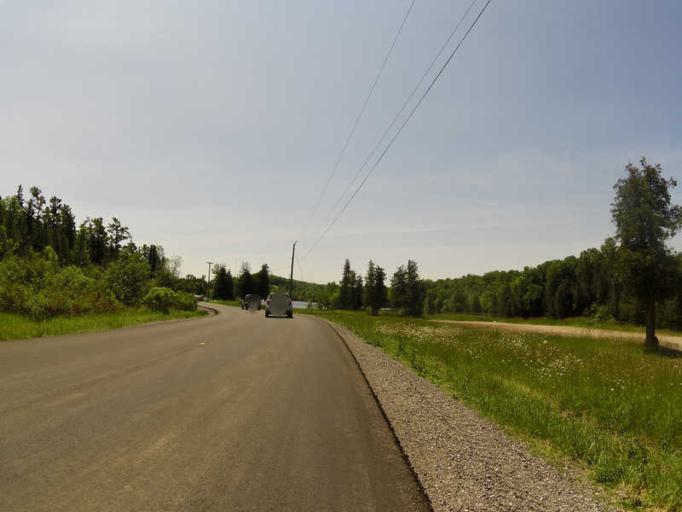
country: CA
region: Ontario
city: Peterborough
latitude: 44.3705
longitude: -78.2902
